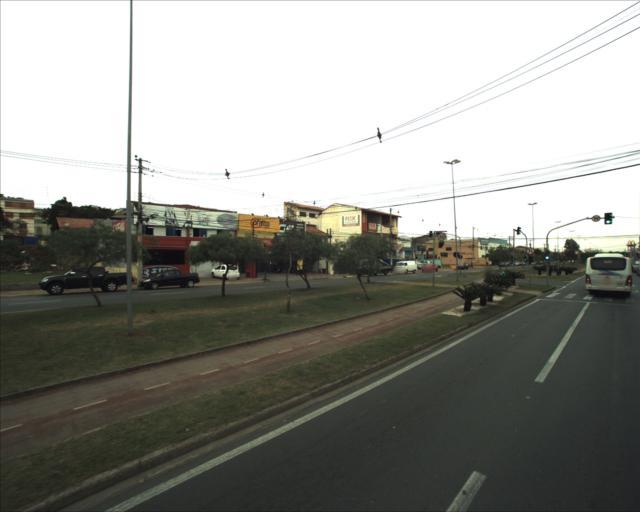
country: BR
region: Sao Paulo
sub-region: Sorocaba
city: Sorocaba
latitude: -23.4921
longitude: -47.5079
